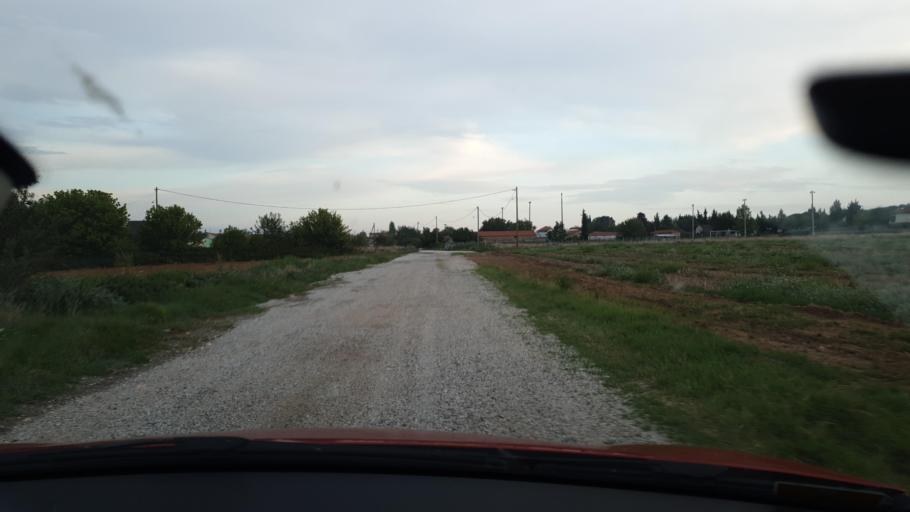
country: GR
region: Central Macedonia
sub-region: Nomos Kilkis
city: Kristoni
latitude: 40.9560
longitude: 22.8199
